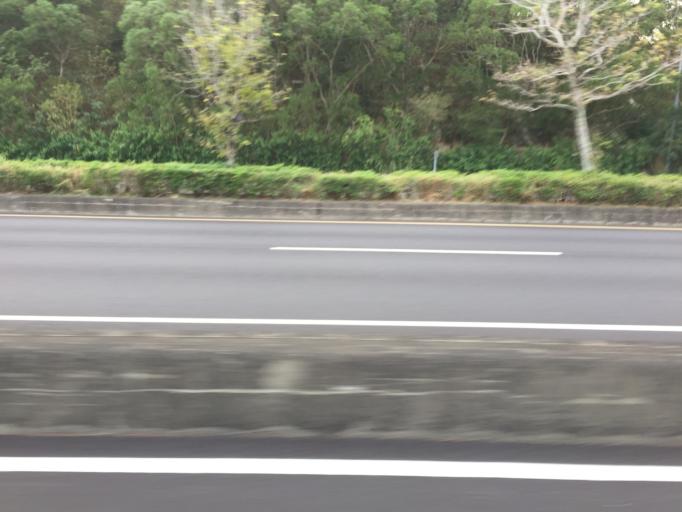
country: TW
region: Taiwan
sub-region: Hsinchu
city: Hsinchu
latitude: 24.7677
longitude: 120.9543
